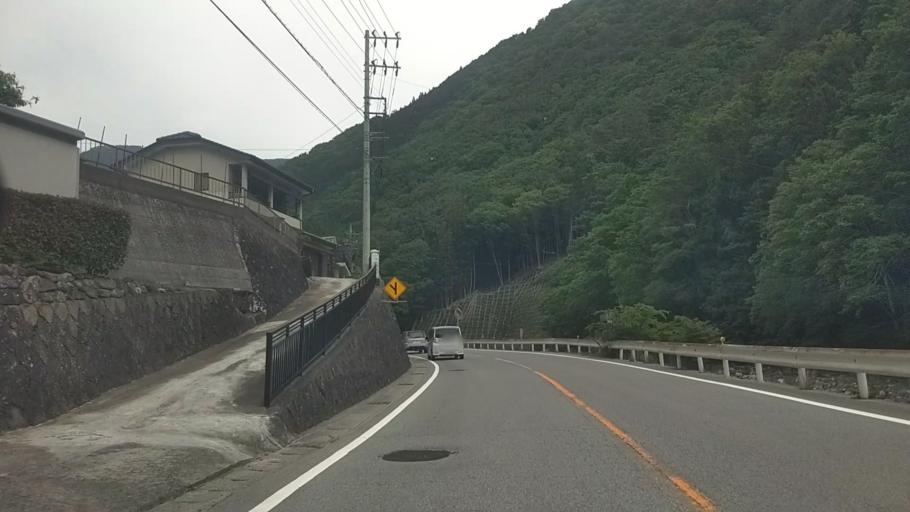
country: JP
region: Yamanashi
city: Fujikawaguchiko
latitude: 35.5318
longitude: 138.6072
